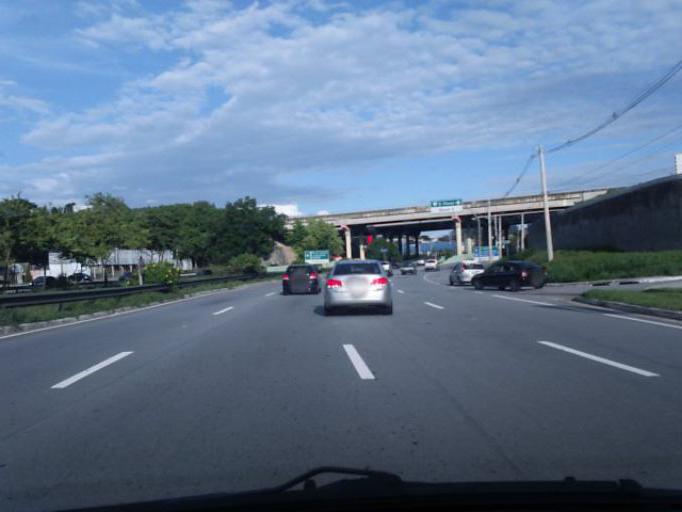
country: BR
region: Sao Paulo
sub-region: Sao Jose Dos Campos
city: Sao Jose dos Campos
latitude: -23.2114
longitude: -45.8932
